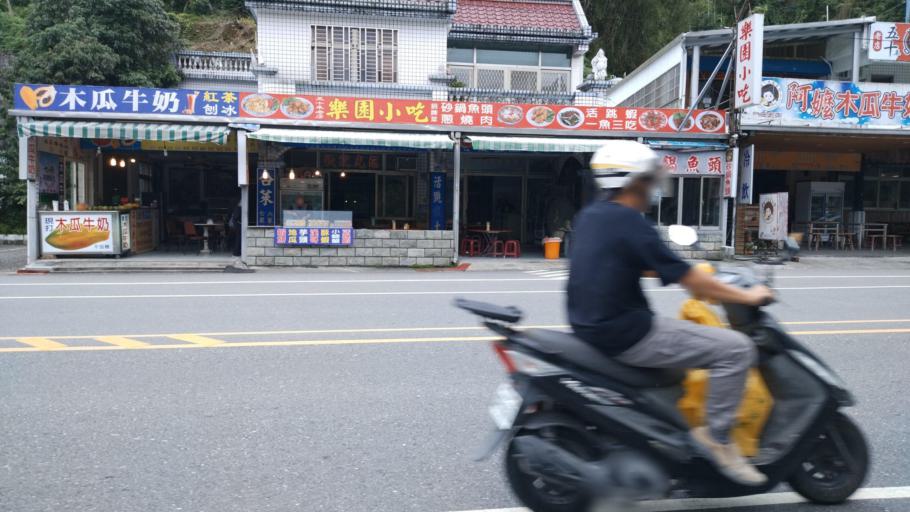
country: TW
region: Taiwan
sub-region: Hualien
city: Hualian
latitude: 23.9281
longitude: 121.5057
